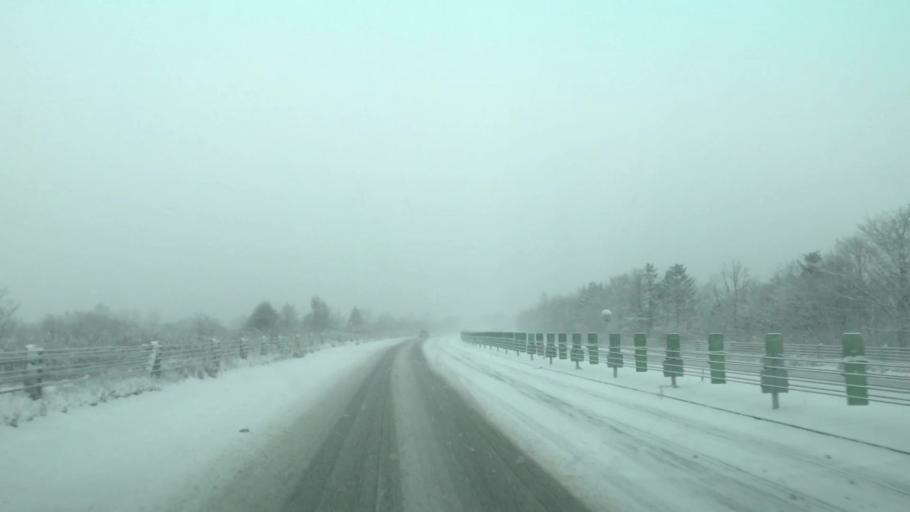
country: JP
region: Hokkaido
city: Shiraoi
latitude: 42.5043
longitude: 141.2676
